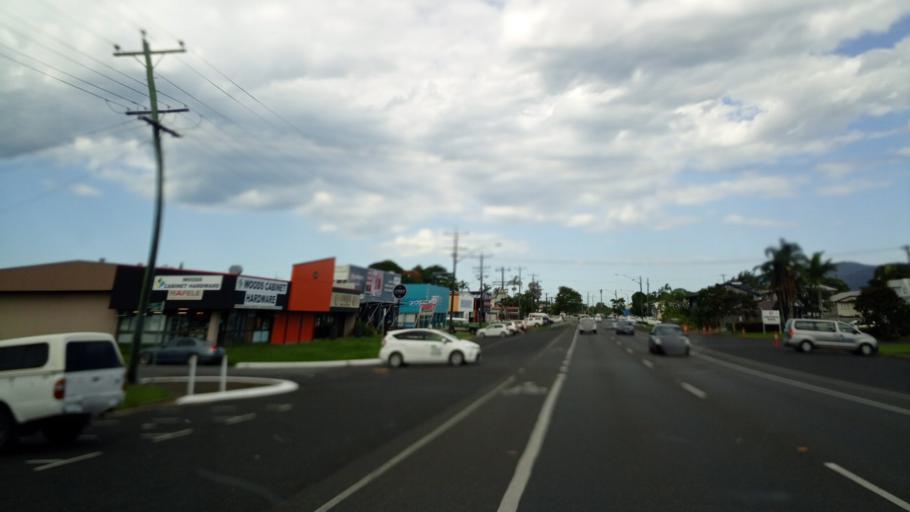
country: AU
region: Queensland
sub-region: Cairns
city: Cairns
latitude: -16.9356
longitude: 145.7580
